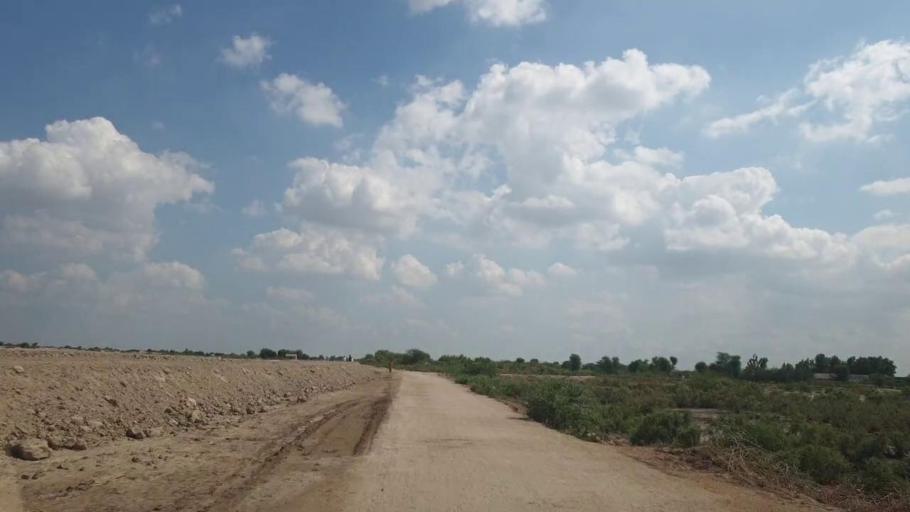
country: PK
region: Sindh
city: Pithoro
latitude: 25.5868
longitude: 69.3926
